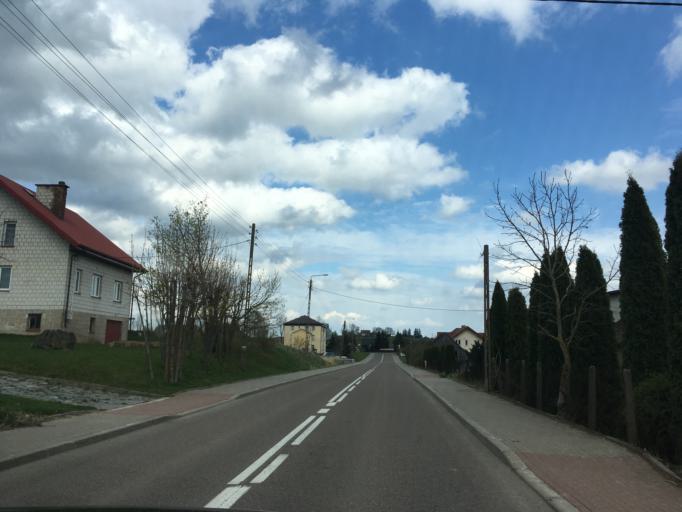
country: PL
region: Podlasie
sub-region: Suwalki
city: Suwalki
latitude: 54.3635
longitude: 22.8644
